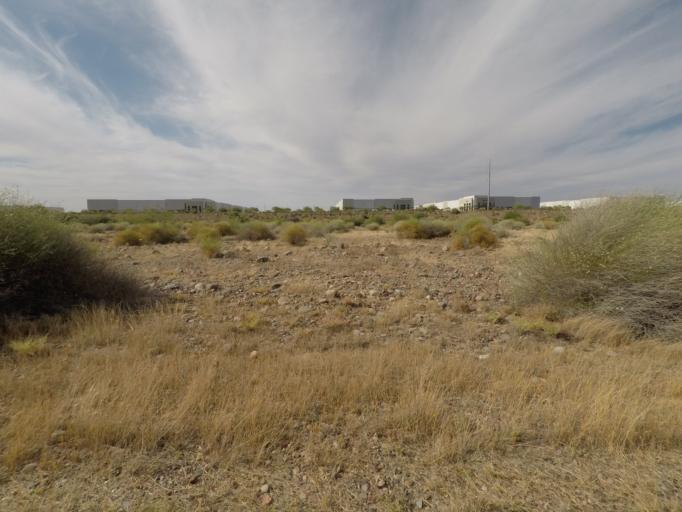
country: US
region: Arizona
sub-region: Maricopa County
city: Phoenix
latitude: 33.4159
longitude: -112.0355
